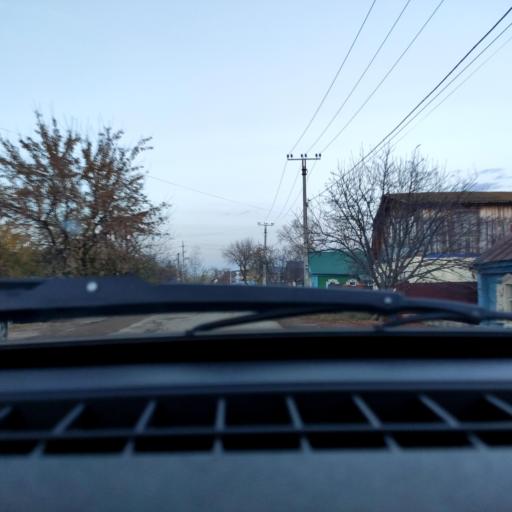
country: RU
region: Bashkortostan
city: Ufa
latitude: 54.7439
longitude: 55.9201
